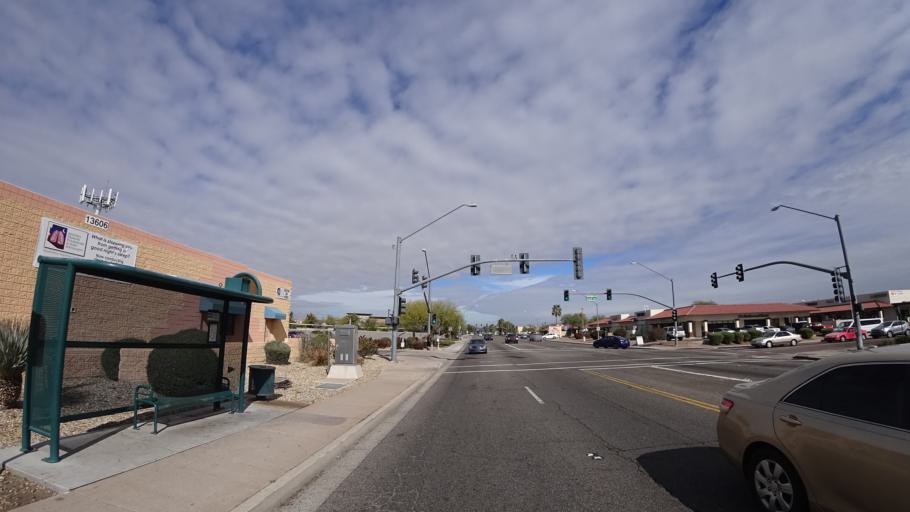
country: US
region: Arizona
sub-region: Maricopa County
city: Peoria
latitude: 33.6087
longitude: -112.1860
